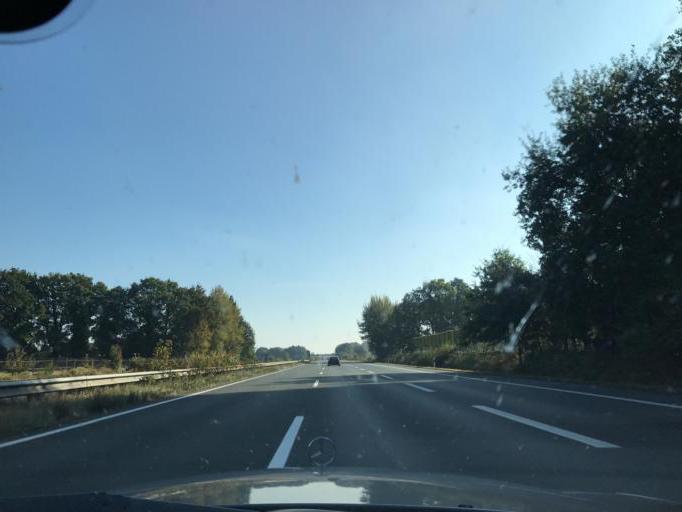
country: DE
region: Lower Saxony
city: Wiefelstede
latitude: 53.1875
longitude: 8.1047
